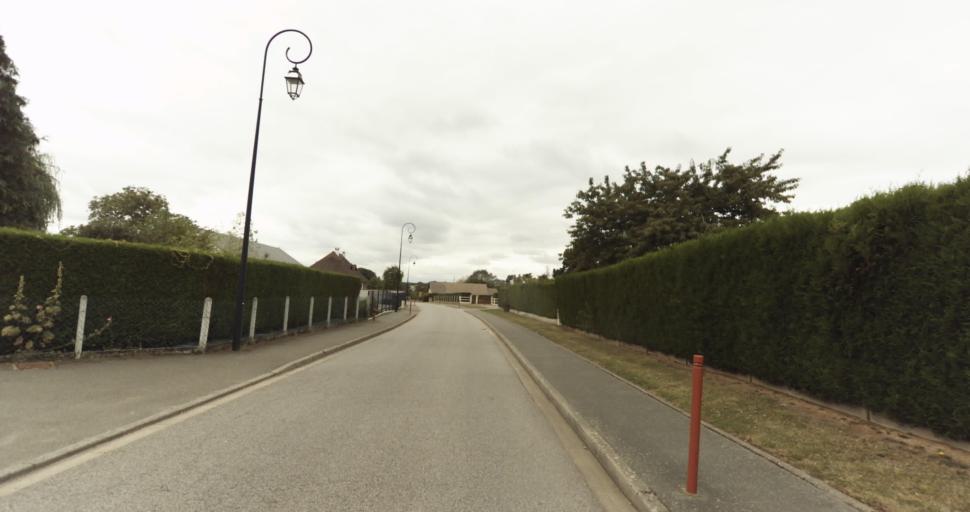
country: FR
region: Haute-Normandie
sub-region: Departement de l'Eure
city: Gravigny
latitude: 49.0302
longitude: 1.1994
